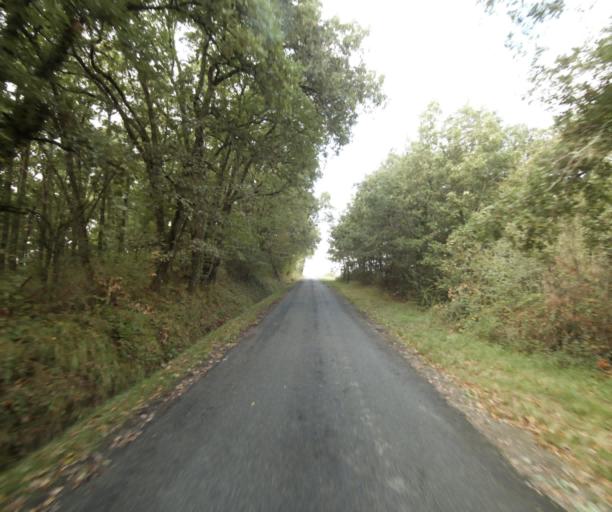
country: FR
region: Midi-Pyrenees
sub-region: Departement du Tarn-et-Garonne
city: Beaumont-de-Lomagne
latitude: 43.8758
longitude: 1.0850
